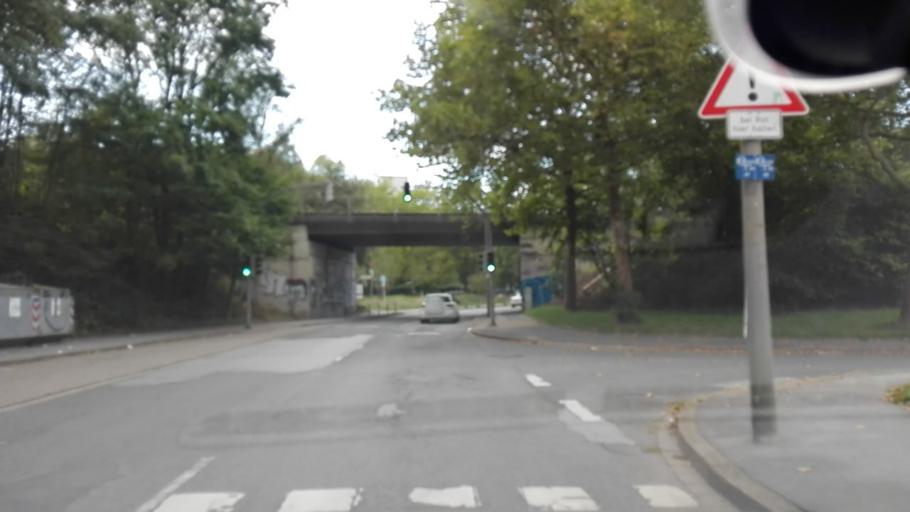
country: DE
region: North Rhine-Westphalia
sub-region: Regierungsbezirk Arnsberg
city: Dortmund
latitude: 51.4901
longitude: 7.4333
